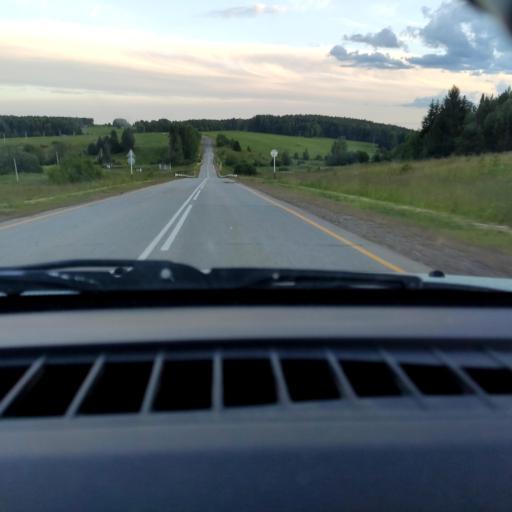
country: RU
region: Perm
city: Kukushtan
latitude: 57.3070
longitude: 56.5400
